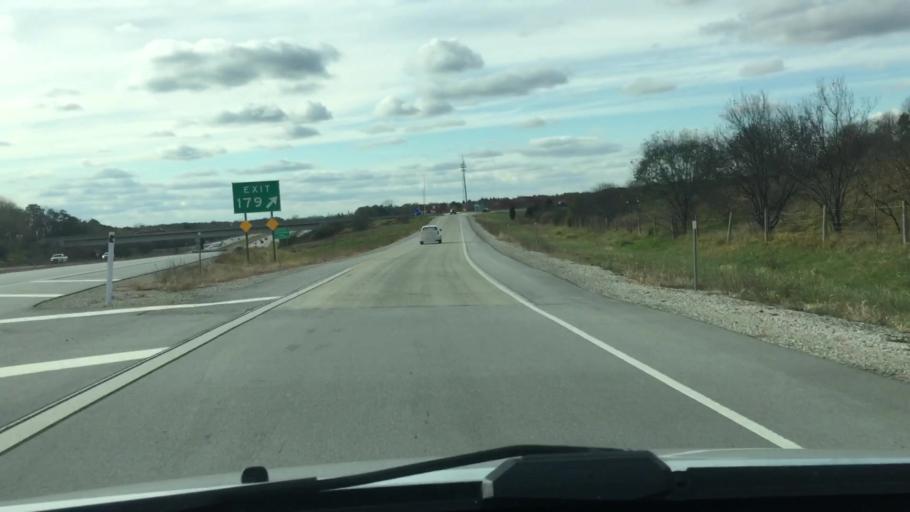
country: US
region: Wisconsin
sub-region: Waukesha County
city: Nashotah
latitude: 43.1021
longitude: -88.3993
